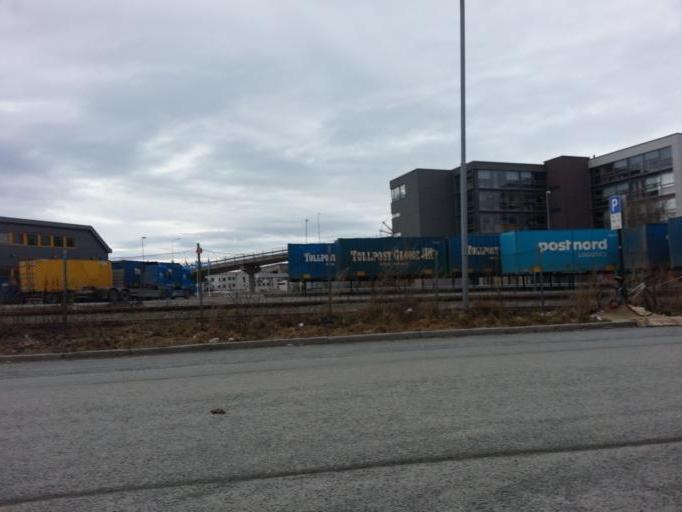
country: NO
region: Sor-Trondelag
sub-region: Trondheim
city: Trondheim
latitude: 63.4380
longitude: 10.4214
